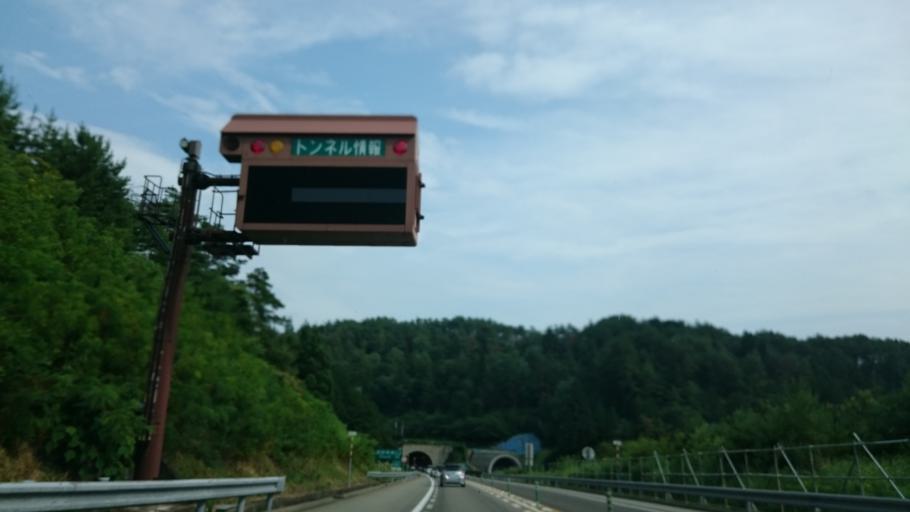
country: JP
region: Gifu
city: Gujo
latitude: 35.8975
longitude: 136.8794
